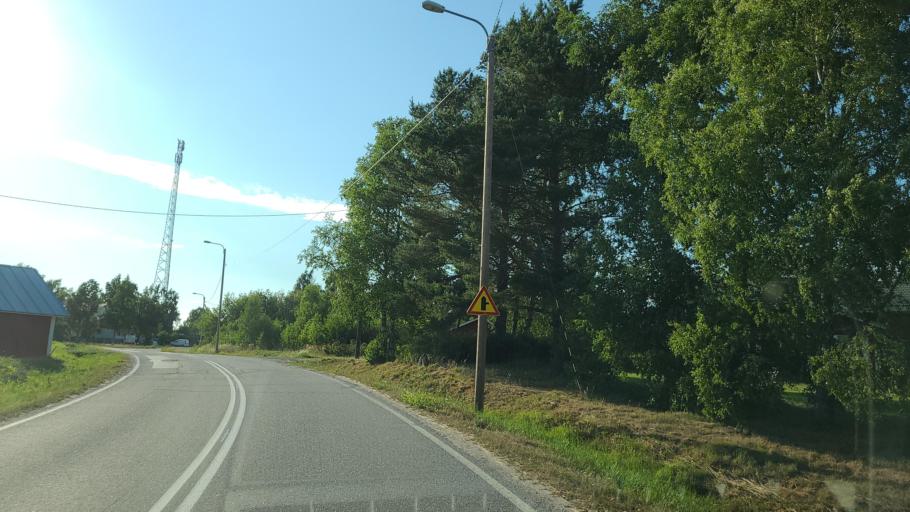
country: FI
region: Ostrobothnia
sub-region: Vaasa
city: Replot
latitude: 63.3428
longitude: 21.3287
